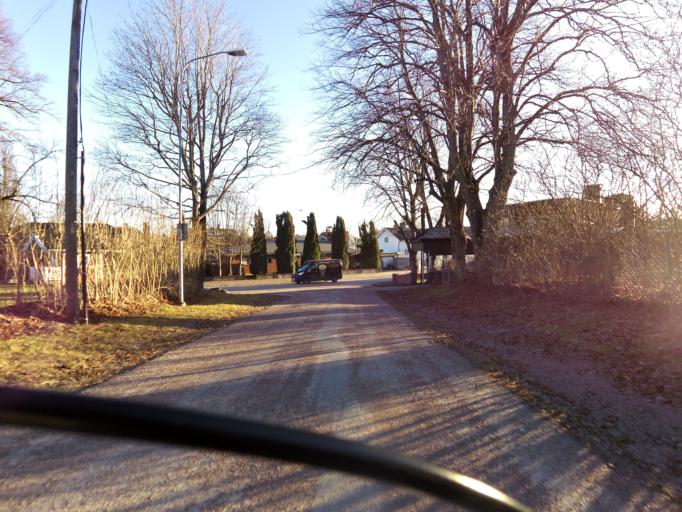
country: SE
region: Gaevleborg
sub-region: Gavle Kommun
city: Gavle
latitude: 60.6714
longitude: 17.1277
